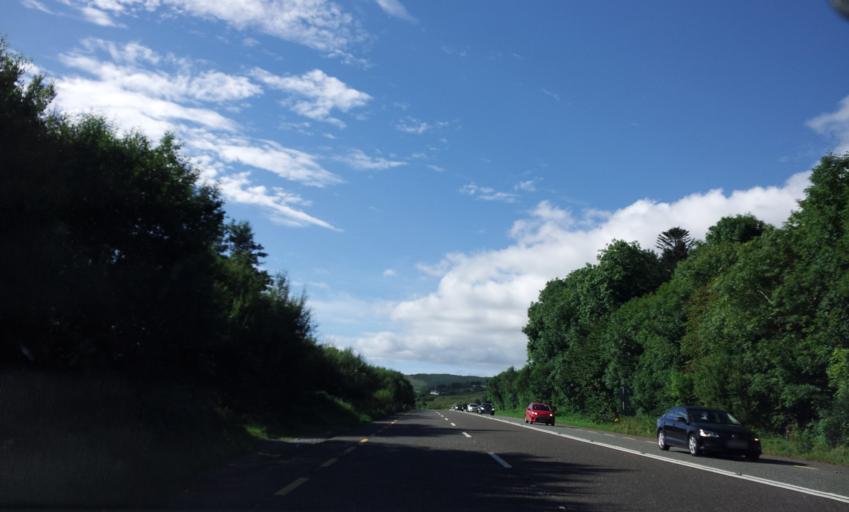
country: IE
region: Munster
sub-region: County Cork
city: Millstreet
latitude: 51.9541
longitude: -9.1866
